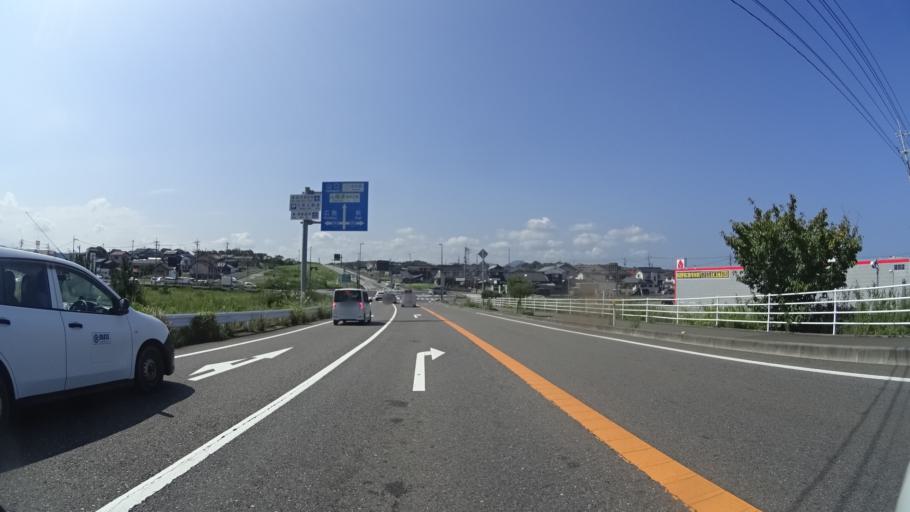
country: JP
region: Shimane
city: Masuda
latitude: 34.6888
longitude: 131.8253
